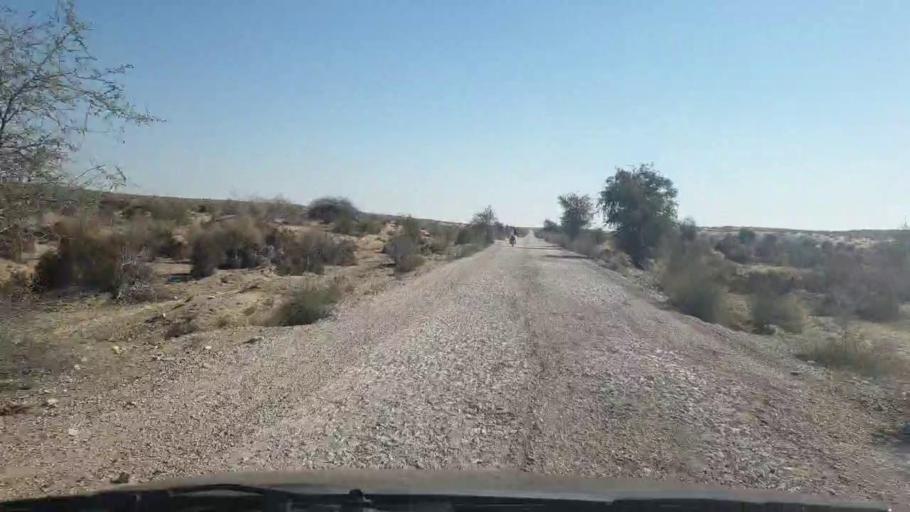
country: PK
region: Sindh
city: Bozdar
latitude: 27.0317
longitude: 68.7027
